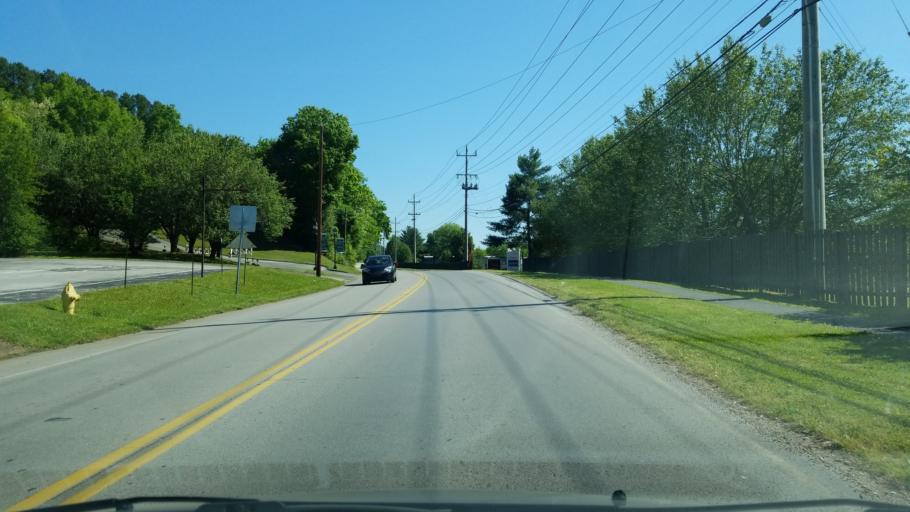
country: US
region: Tennessee
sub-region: Hamilton County
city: Signal Mountain
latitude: 35.1079
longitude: -85.3256
